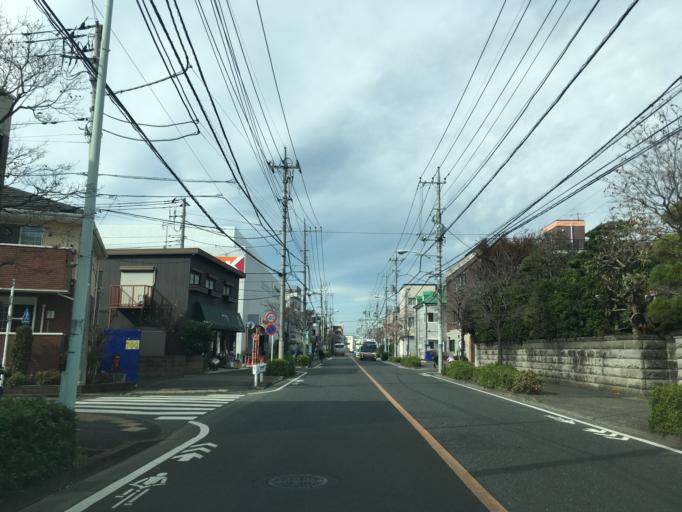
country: JP
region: Tokyo
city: Chofugaoka
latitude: 35.6394
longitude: 139.5722
